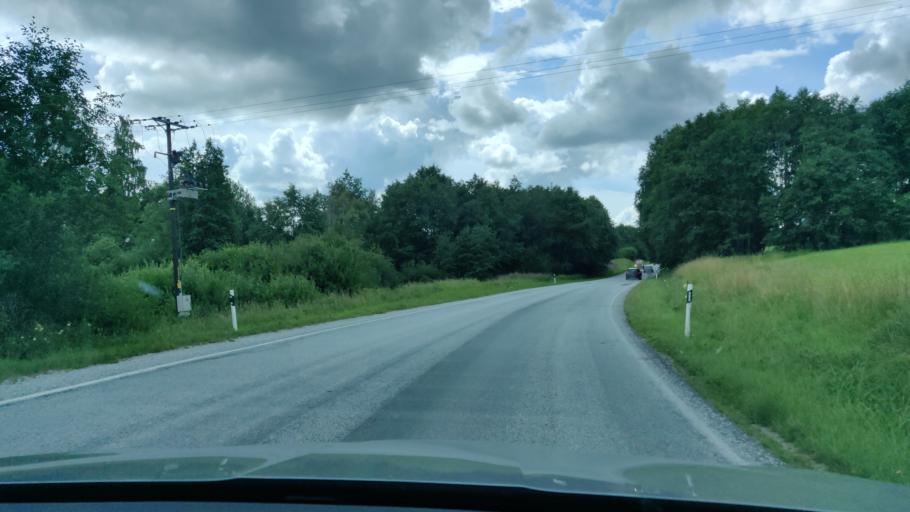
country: EE
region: Vorumaa
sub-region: Antsla vald
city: Vana-Antsla
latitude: 58.0284
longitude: 26.5102
